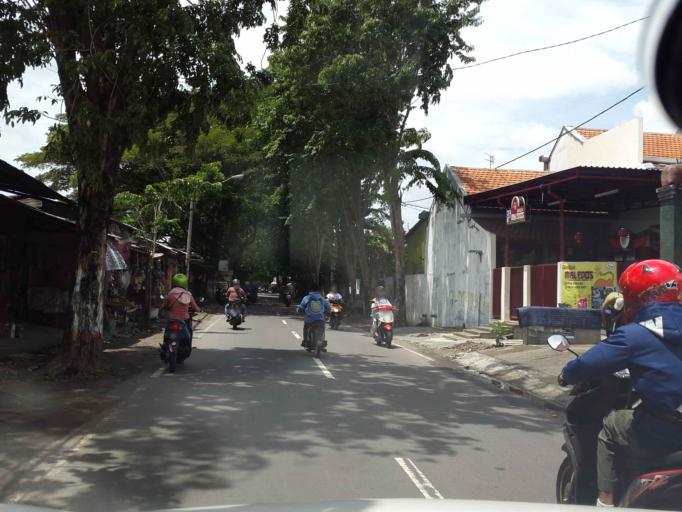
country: ID
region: East Java
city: Mojokerto
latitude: -7.4592
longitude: 112.4483
